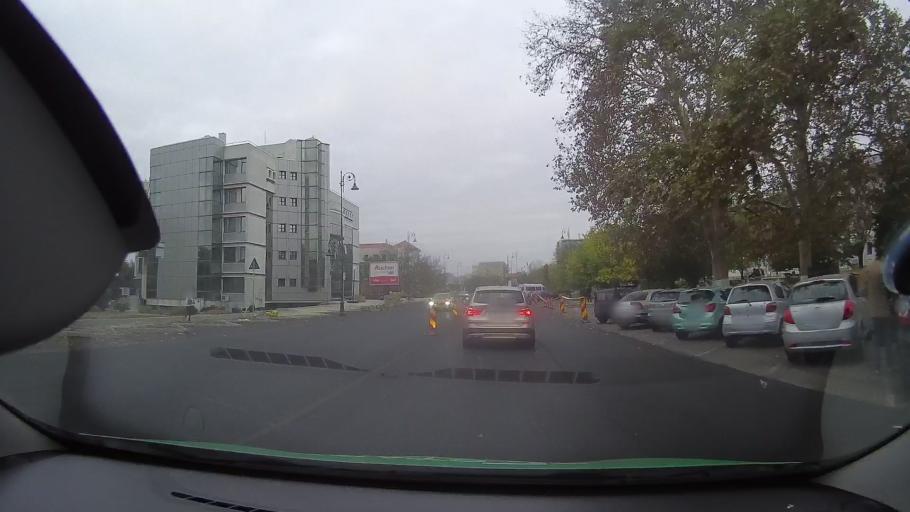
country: RO
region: Constanta
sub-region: Municipiul Constanta
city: Constanta
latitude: 44.1765
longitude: 28.6533
